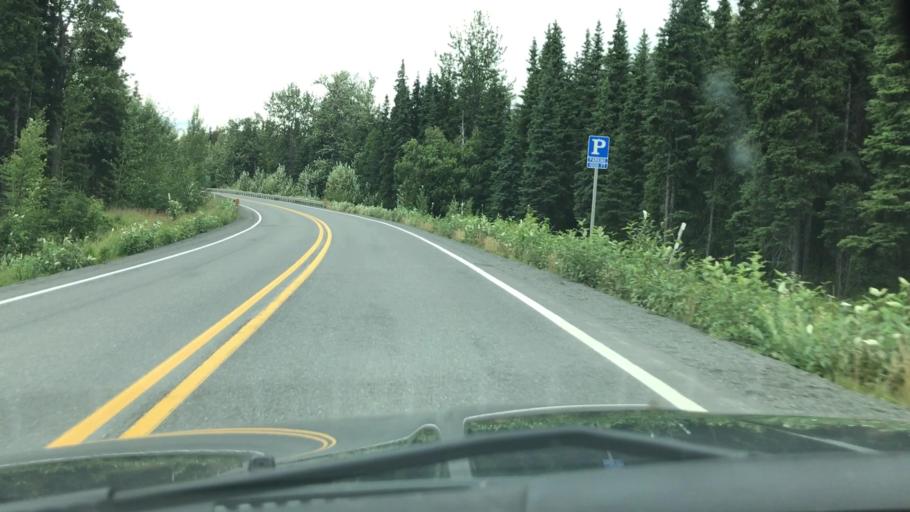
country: US
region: Alaska
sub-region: Kenai Peninsula Borough
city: Seward
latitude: 60.4839
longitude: -149.9461
